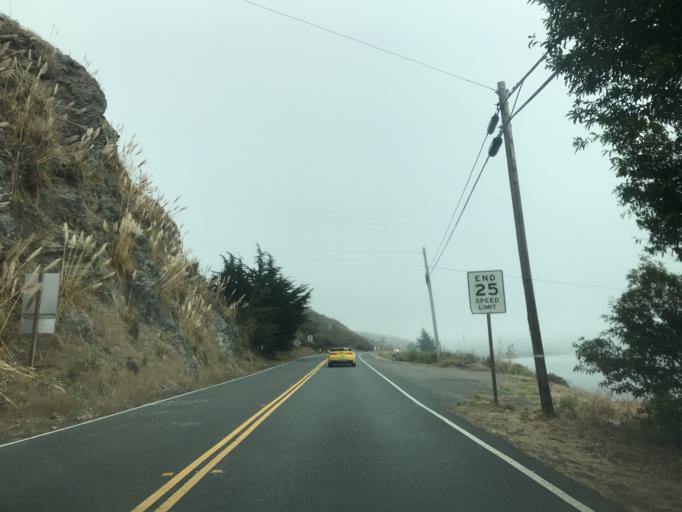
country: US
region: California
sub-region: Sonoma County
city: Monte Rio
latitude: 38.4480
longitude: -123.1139
